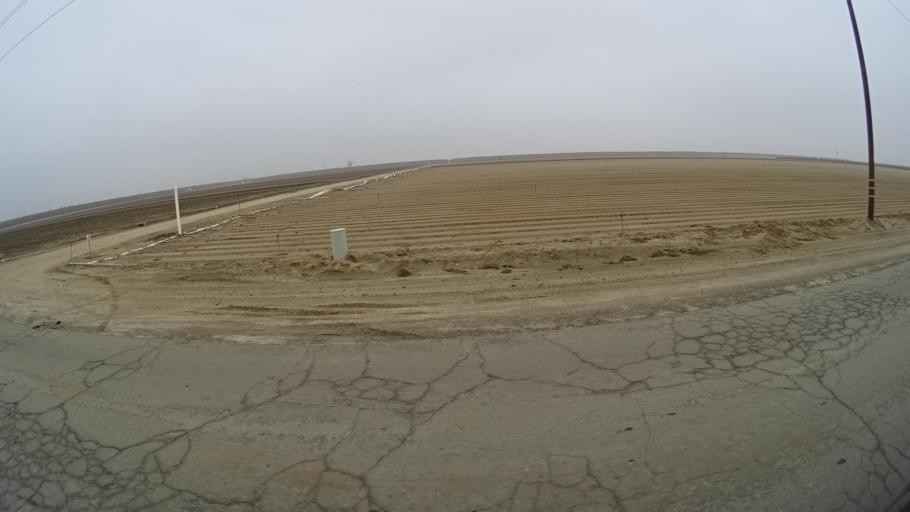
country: US
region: California
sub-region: Kern County
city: Wasco
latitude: 35.6048
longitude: -119.5091
